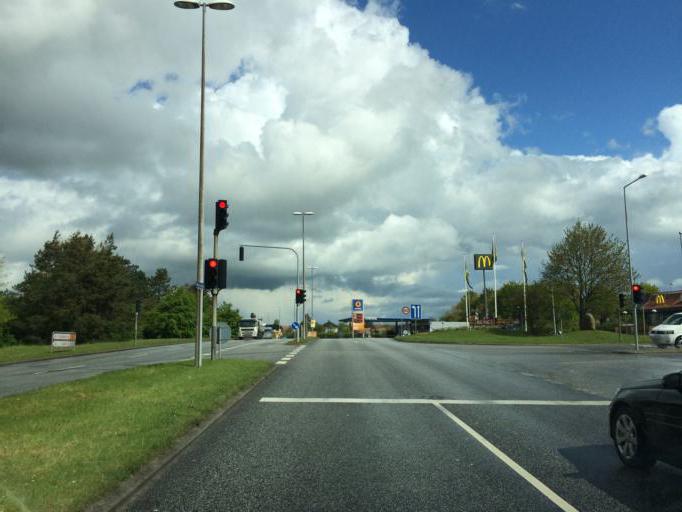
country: DK
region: Central Jutland
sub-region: Holstebro Kommune
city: Holstebro
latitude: 56.3627
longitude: 8.6117
